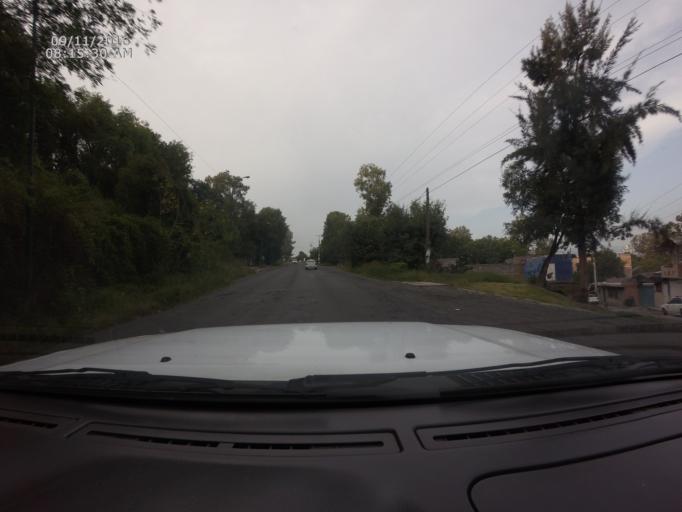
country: MX
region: Michoacan
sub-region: Morelia
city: Morelos
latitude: 19.6548
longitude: -101.2303
